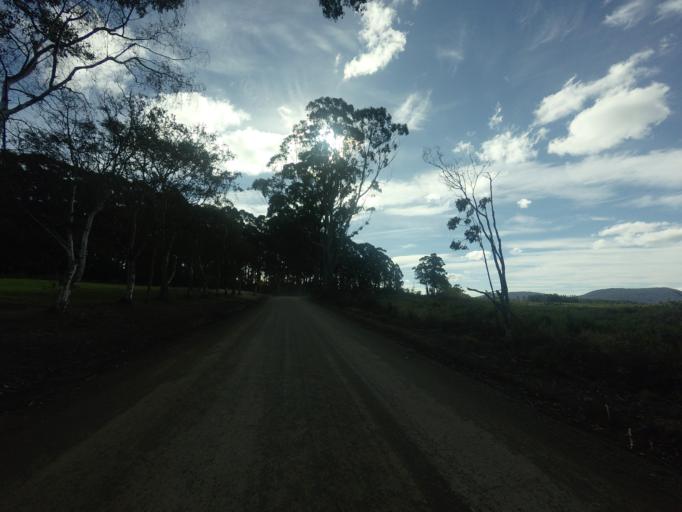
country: AU
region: Tasmania
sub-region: Clarence
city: Sandford
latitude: -43.1692
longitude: 147.7684
